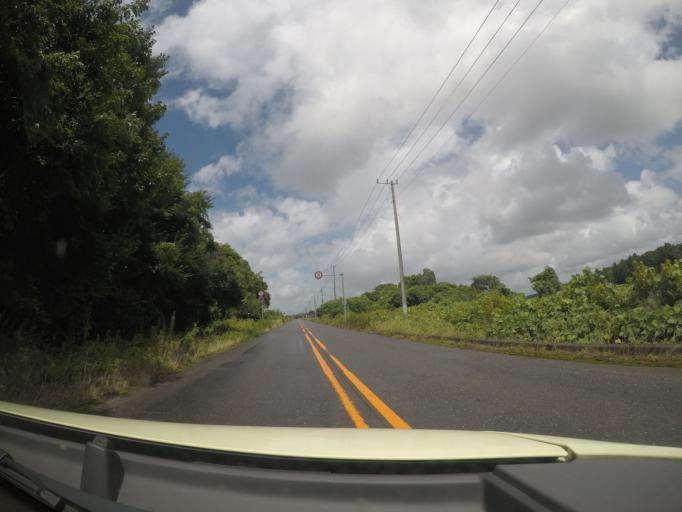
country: JP
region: Ibaraki
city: Ishige
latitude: 36.0773
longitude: 140.0247
